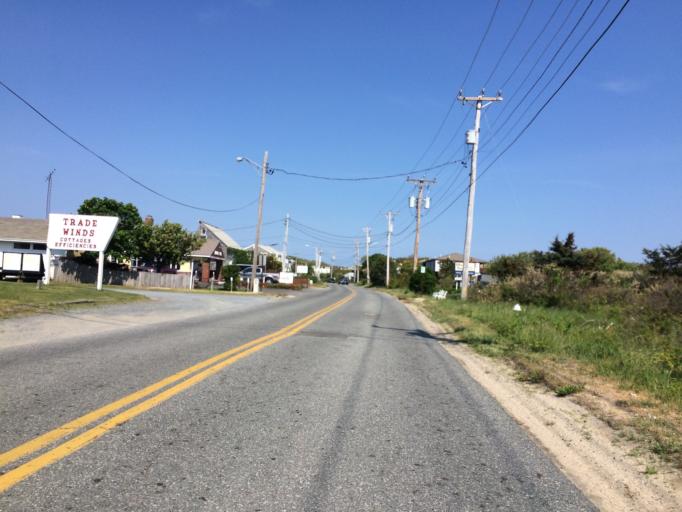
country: US
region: Massachusetts
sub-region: Barnstable County
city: Provincetown
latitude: 42.0627
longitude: -70.1455
